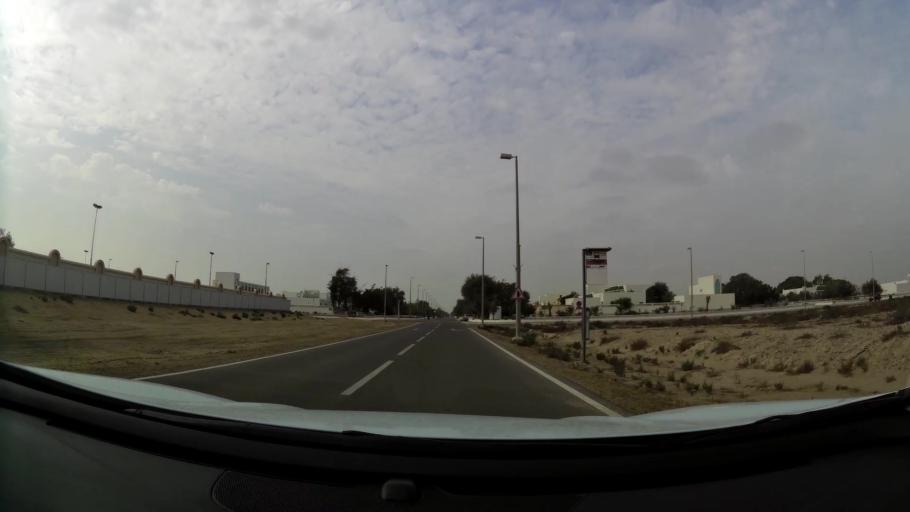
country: AE
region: Abu Dhabi
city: Abu Dhabi
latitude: 24.6432
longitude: 54.7291
